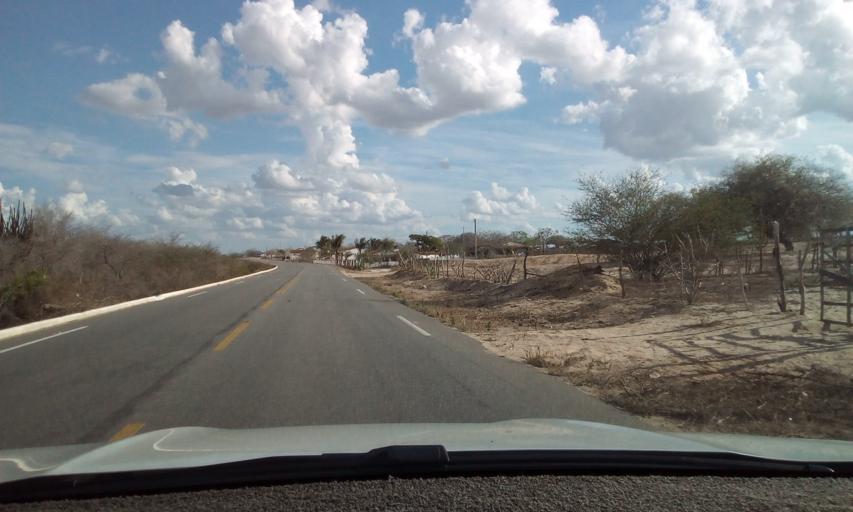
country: BR
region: Paraiba
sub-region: Soledade
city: Soledade
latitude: -6.8913
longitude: -36.3979
